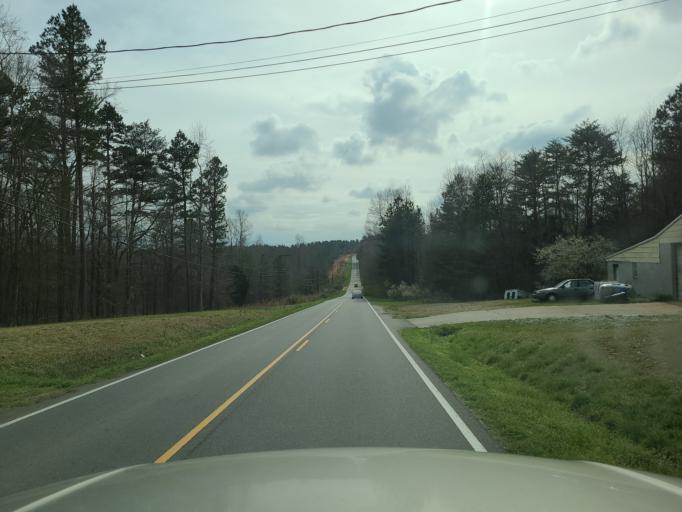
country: US
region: North Carolina
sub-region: Cleveland County
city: Boiling Springs
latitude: 35.2515
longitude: -81.7119
